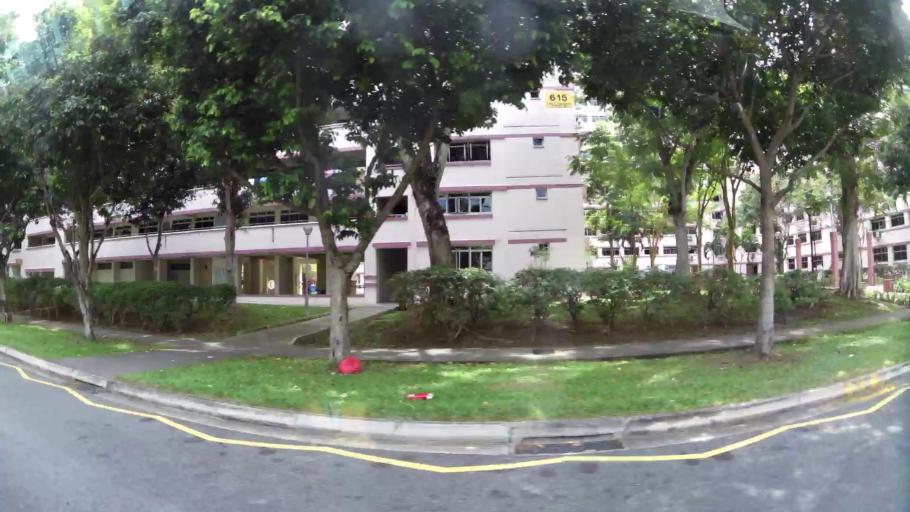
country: MY
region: Johor
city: Johor Bahru
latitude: 1.4012
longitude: 103.7448
